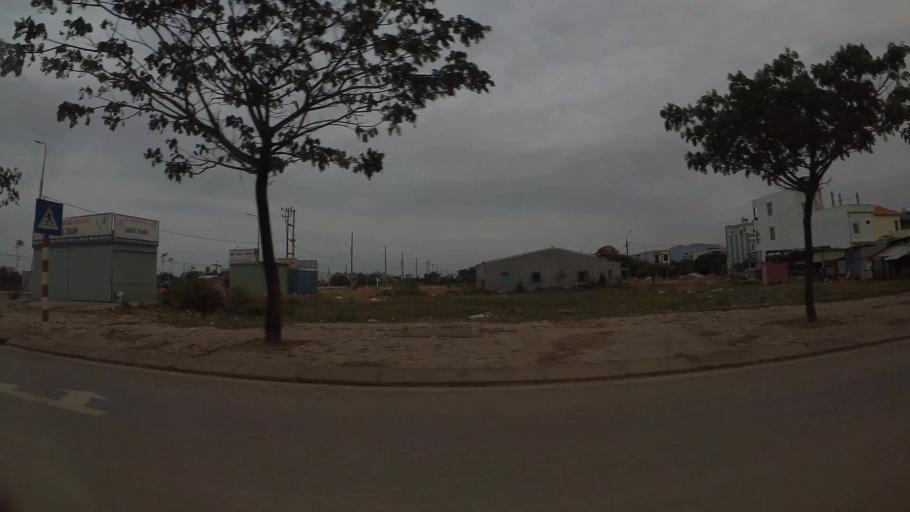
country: VN
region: Da Nang
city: Lien Chieu
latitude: 16.1064
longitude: 108.1261
